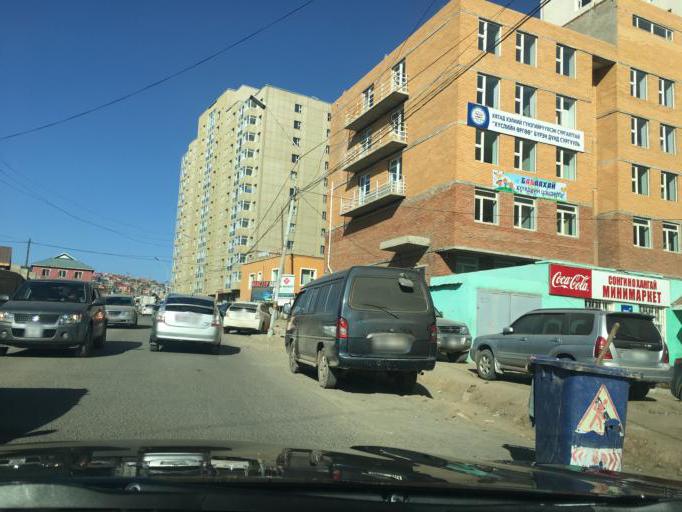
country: MN
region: Ulaanbaatar
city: Ulaanbaatar
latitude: 47.9273
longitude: 106.8770
